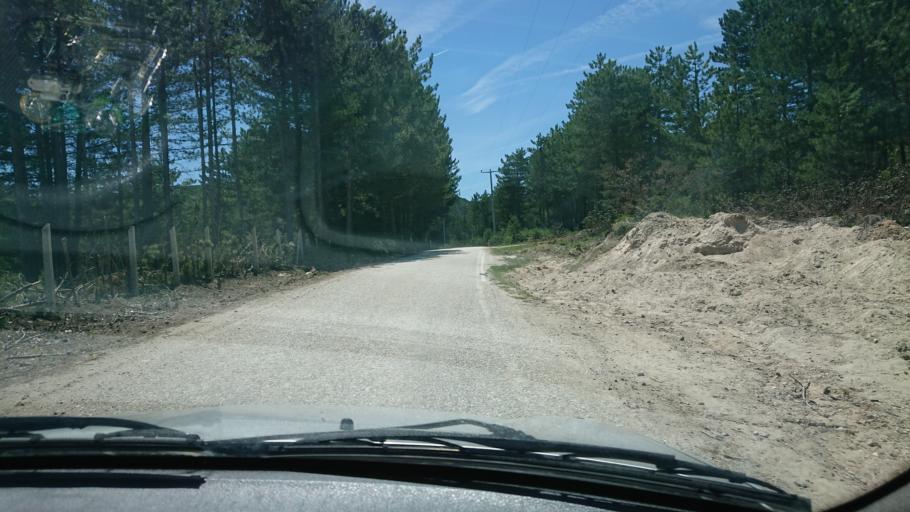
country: TR
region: Kuetahya
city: Sabuncu
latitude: 39.5230
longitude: 30.4300
